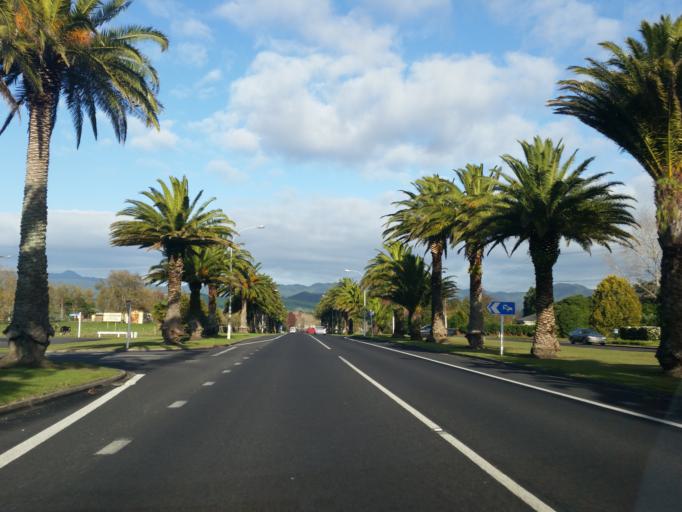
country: NZ
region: Waikato
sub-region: Hauraki District
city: Waihi
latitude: -37.3970
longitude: 175.8278
